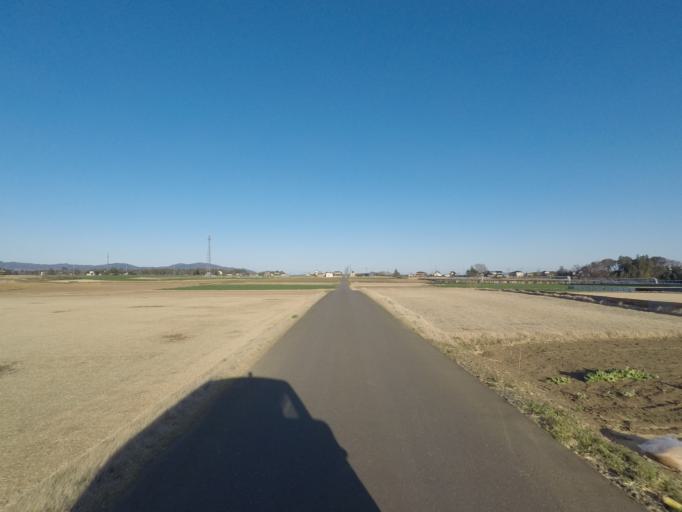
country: JP
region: Ibaraki
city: Ishige
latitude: 36.1347
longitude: 140.0092
